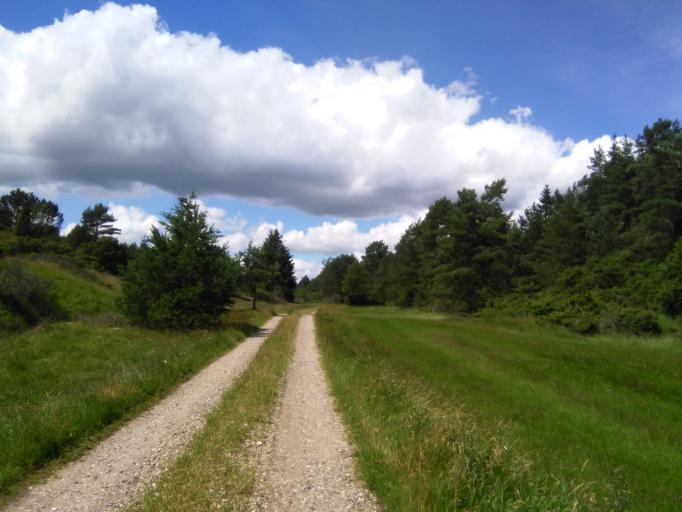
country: DK
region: Central Jutland
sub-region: Silkeborg Kommune
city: Virklund
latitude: 56.0774
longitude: 9.4508
